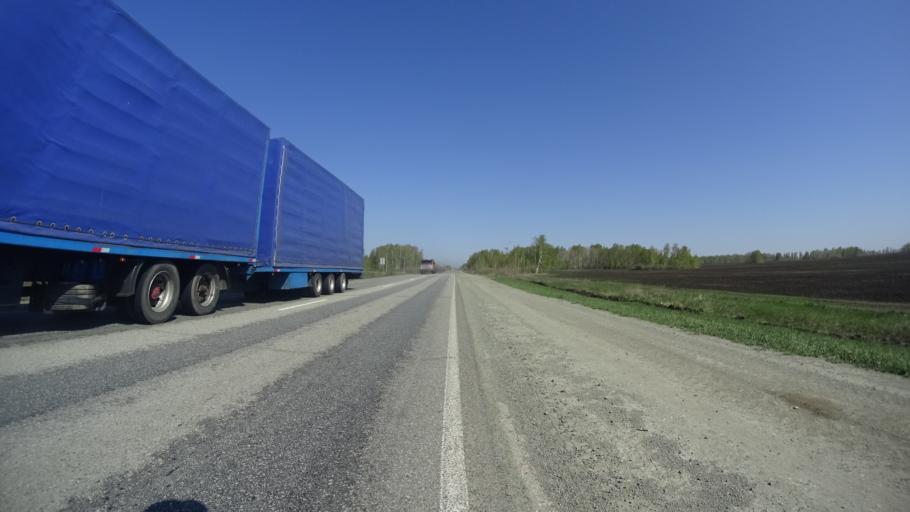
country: RU
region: Chelyabinsk
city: Troitsk
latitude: 54.1812
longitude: 61.4348
